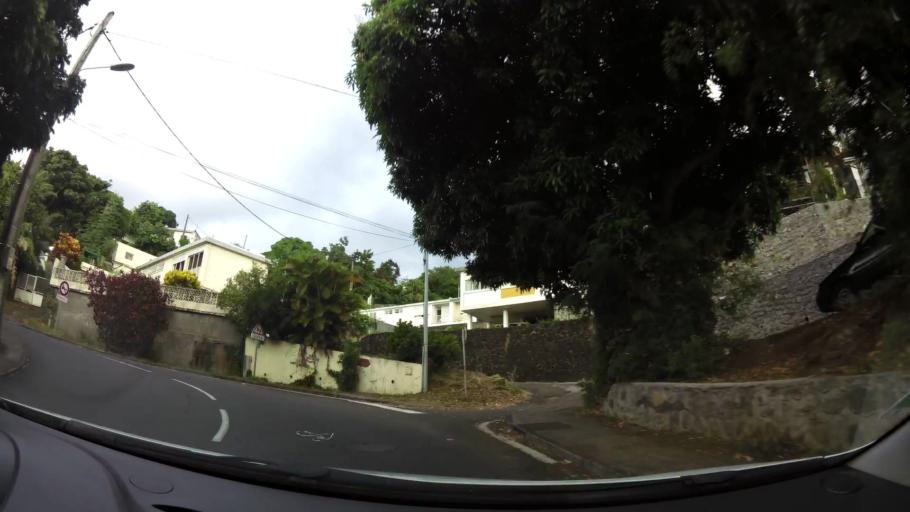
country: RE
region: Reunion
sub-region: Reunion
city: Saint-Denis
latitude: -20.8997
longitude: 55.4440
